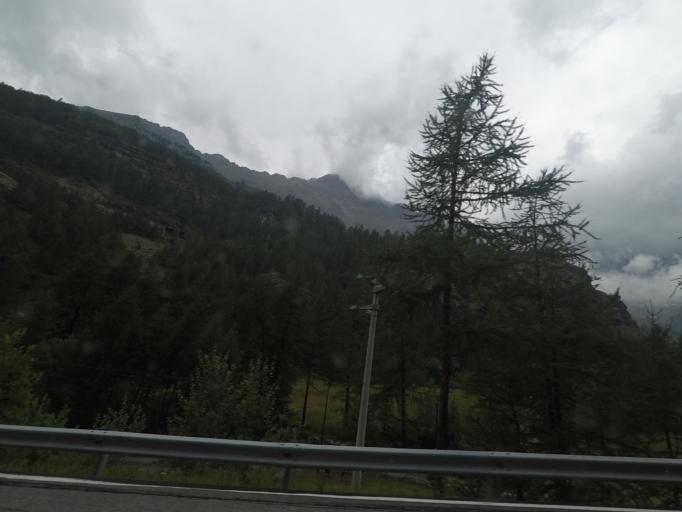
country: IT
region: Aosta Valley
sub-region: Valle d'Aosta
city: Paquier
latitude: 45.9017
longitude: 7.6175
